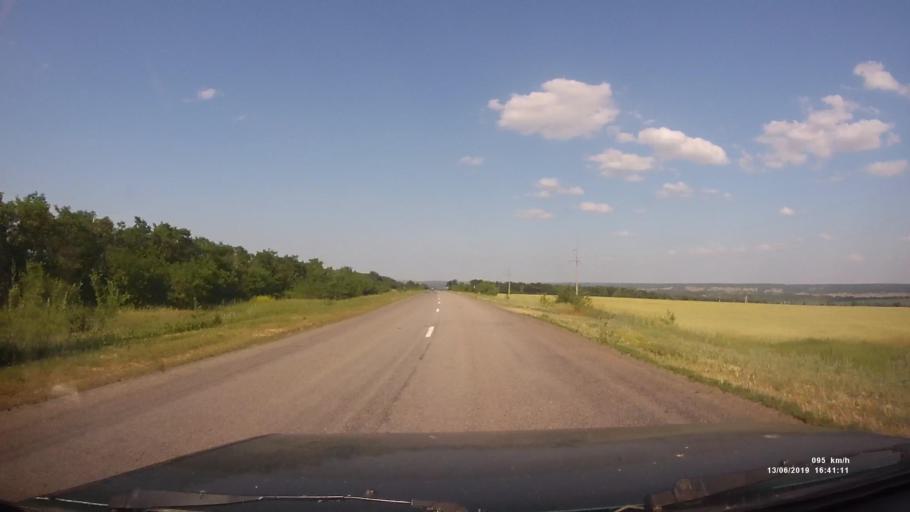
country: RU
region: Rostov
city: Kazanskaya
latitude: 49.9349
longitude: 41.3793
